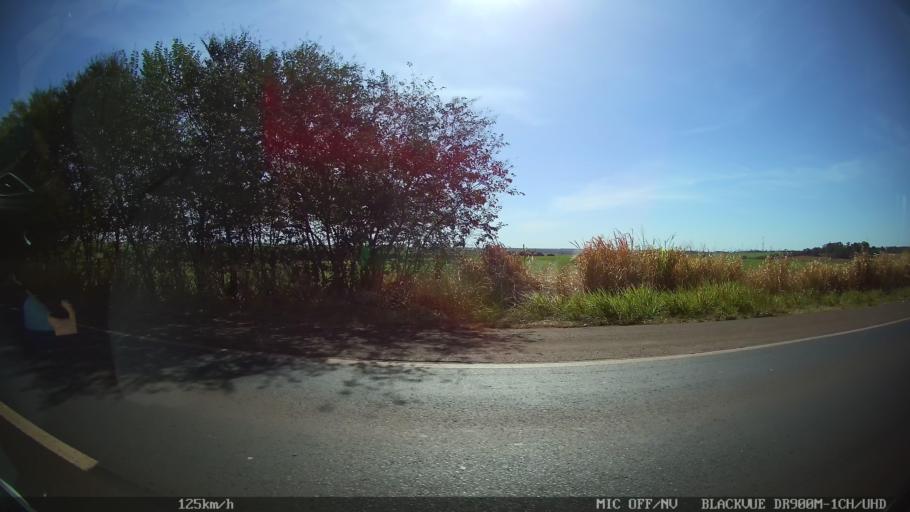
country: BR
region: Sao Paulo
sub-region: Barretos
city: Barretos
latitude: -20.5360
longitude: -48.6066
